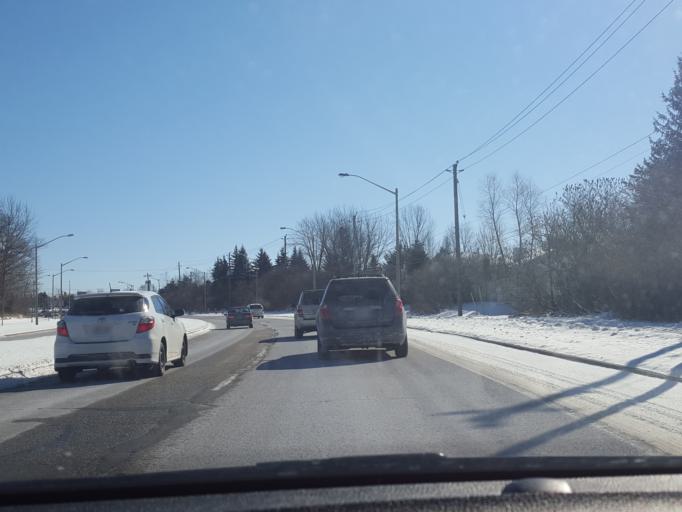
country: CA
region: Ontario
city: Waterloo
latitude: 43.4457
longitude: -80.5480
